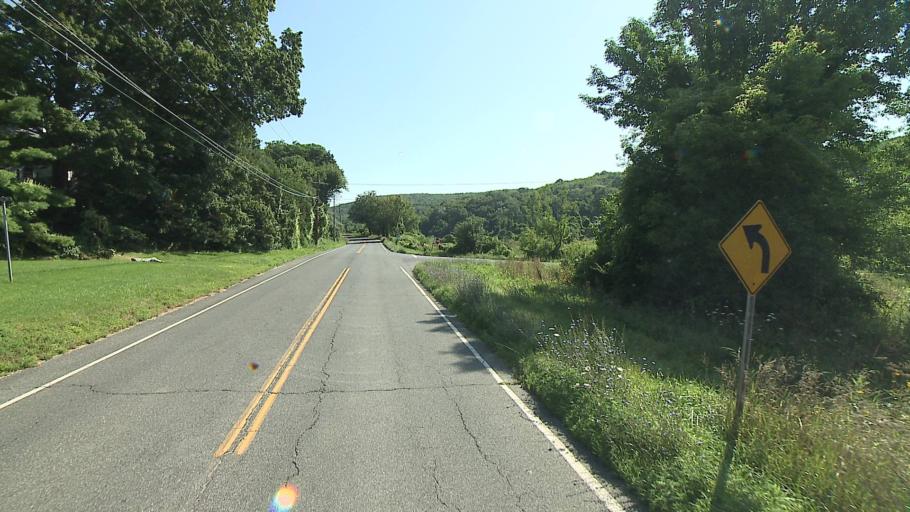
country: US
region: Connecticut
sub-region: Litchfield County
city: Kent
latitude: 41.8914
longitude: -73.4540
